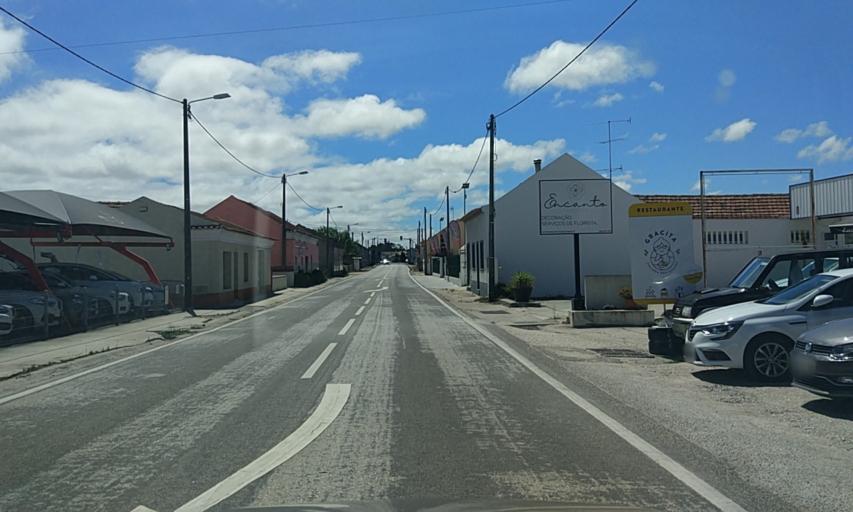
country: PT
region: Aveiro
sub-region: Vagos
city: Vagos
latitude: 40.5322
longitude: -8.6781
